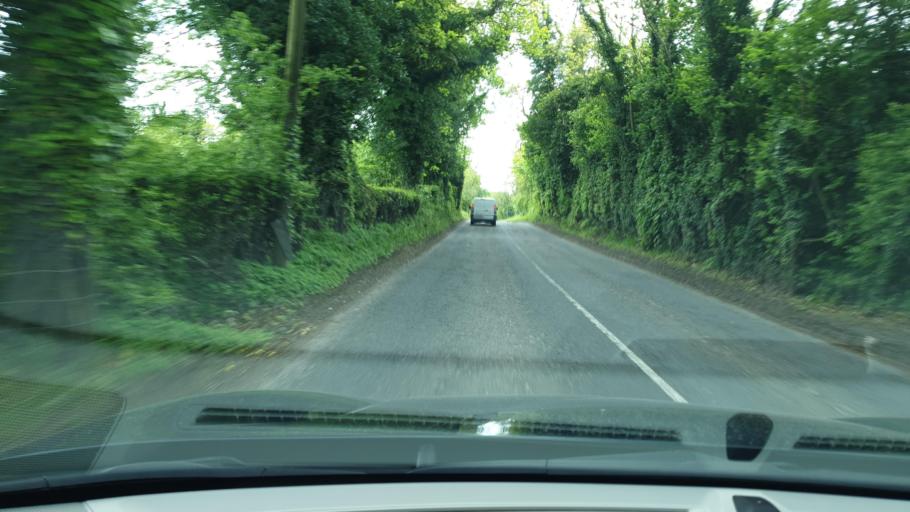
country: IE
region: Ulster
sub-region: An Cabhan
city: Kingscourt
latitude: 53.8340
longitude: -6.7638
